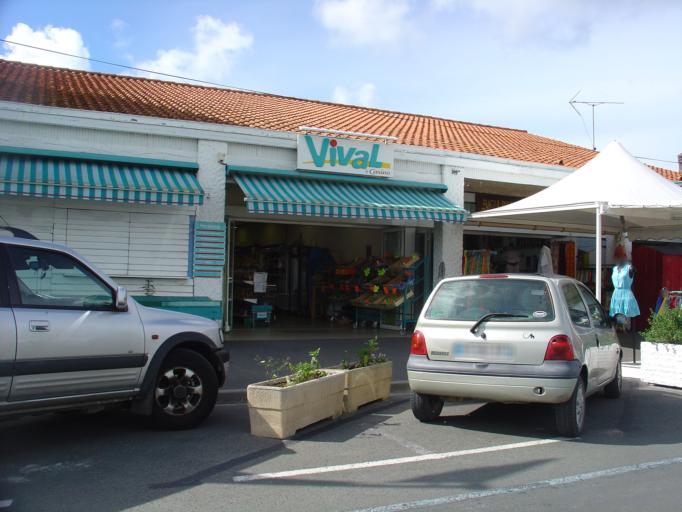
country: FR
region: Poitou-Charentes
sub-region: Departement de la Charente-Maritime
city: Boyard-Ville
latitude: 45.9656
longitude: -1.2428
